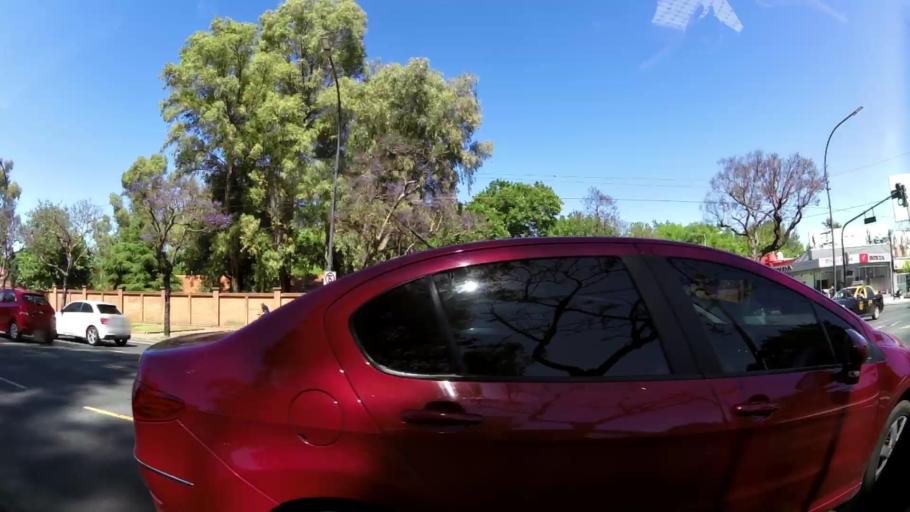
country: AR
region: Buenos Aires
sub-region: Partido de Vicente Lopez
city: Olivos
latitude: -34.5114
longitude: -58.4781
